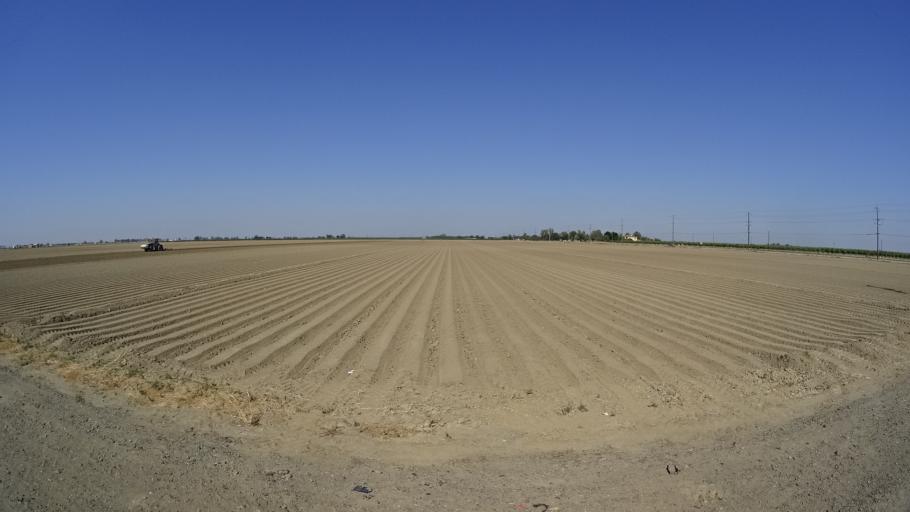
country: US
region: California
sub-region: Kings County
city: Home Garden
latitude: 36.3415
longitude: -119.5653
